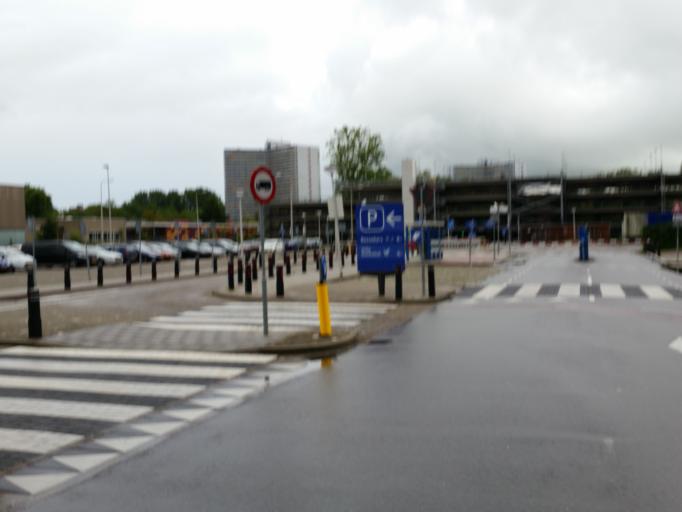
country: NL
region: South Holland
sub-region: Gemeente Delft
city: Delft
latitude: 51.9984
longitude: 4.3412
